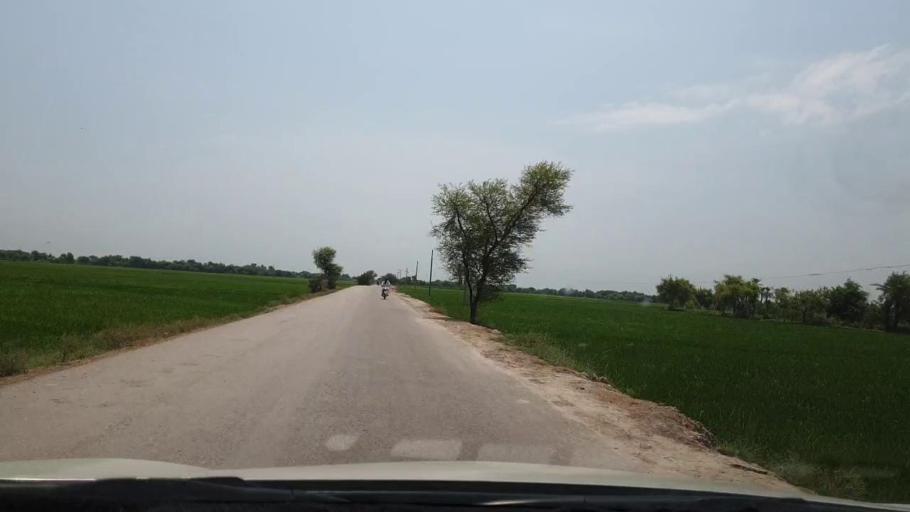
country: PK
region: Sindh
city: Ratodero
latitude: 27.8224
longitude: 68.2433
